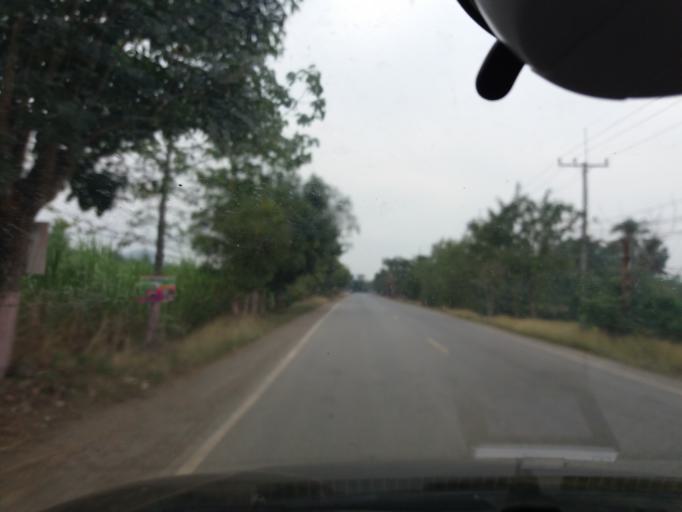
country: TH
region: Suphan Buri
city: Doembang Nangbuat
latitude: 14.8373
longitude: 100.1300
